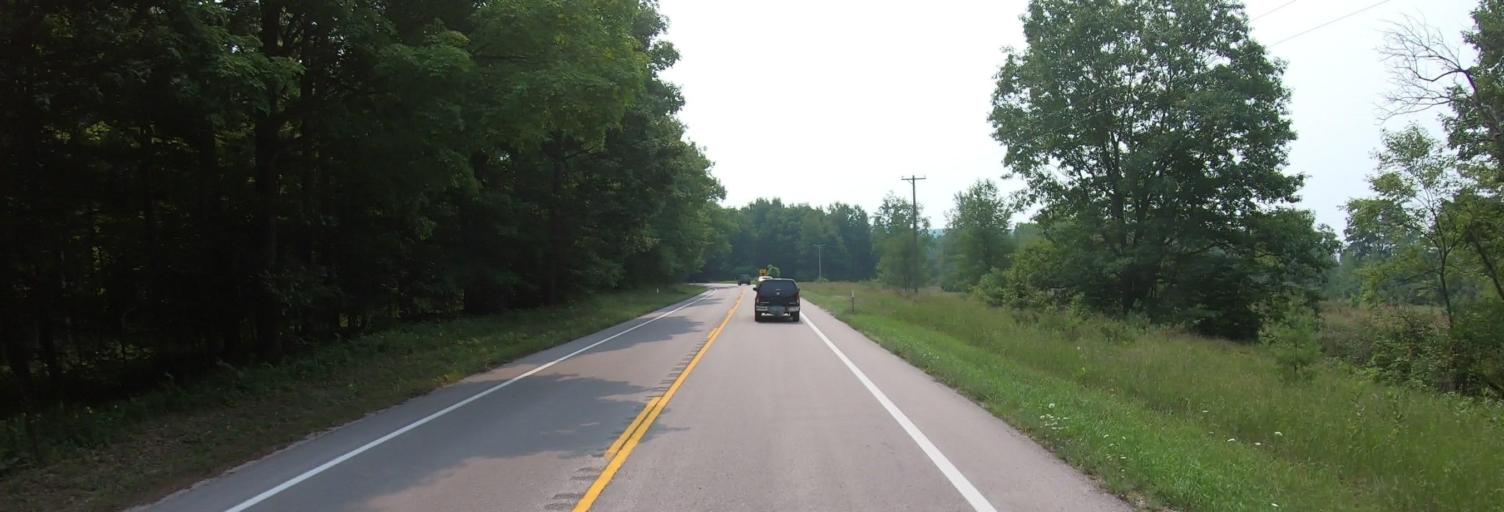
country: US
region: Michigan
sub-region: Leelanau County
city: Leland
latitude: 44.9239
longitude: -85.8799
